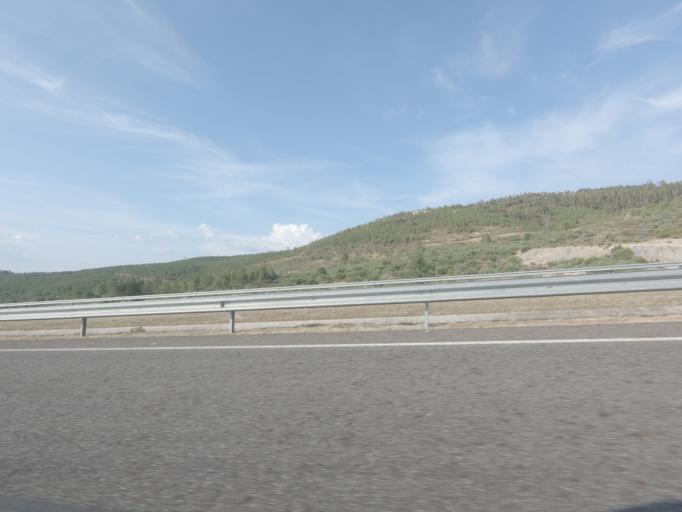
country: ES
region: Galicia
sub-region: Provincia de Ourense
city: Oimbra
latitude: 41.8630
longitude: -7.4277
